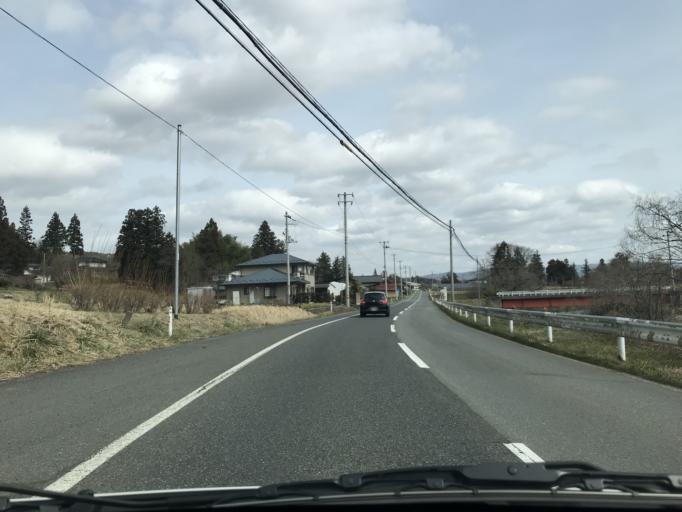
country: JP
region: Iwate
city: Mizusawa
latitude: 39.2139
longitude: 141.2110
